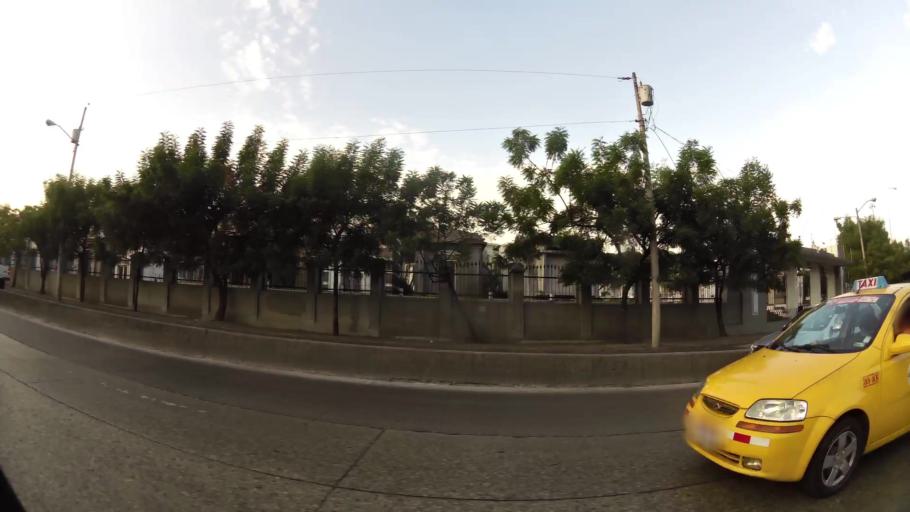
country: EC
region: Guayas
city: Guayaquil
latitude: -2.1834
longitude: -79.8886
